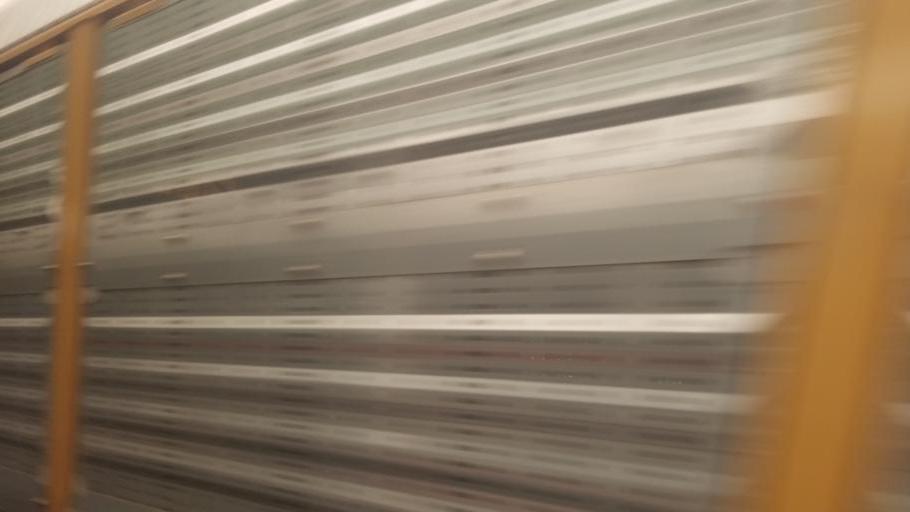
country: US
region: Pennsylvania
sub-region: Somerset County
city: Milford
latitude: 39.8810
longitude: -79.1032
